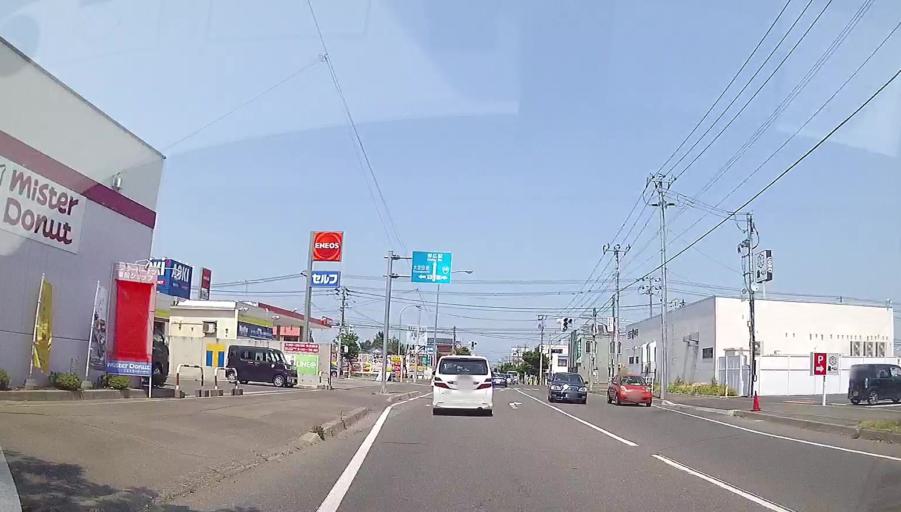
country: JP
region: Hokkaido
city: Obihiro
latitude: 42.8913
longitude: 143.2014
